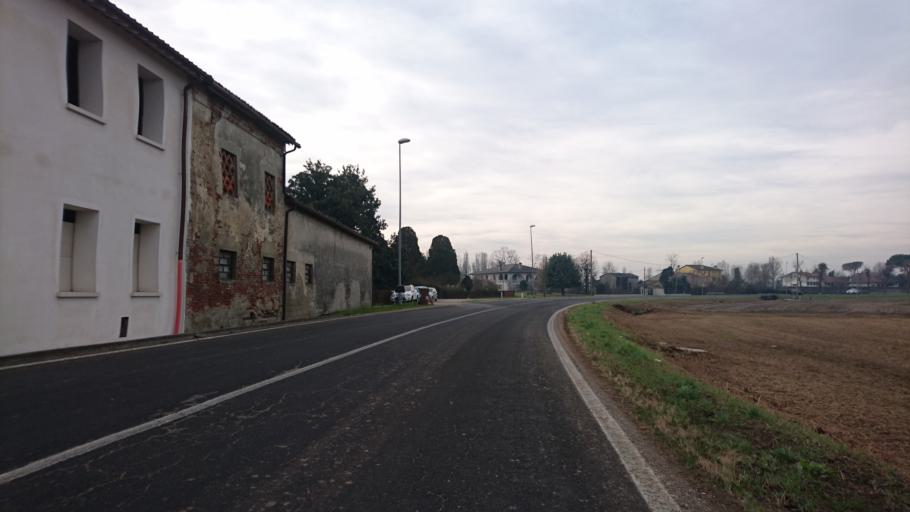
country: IT
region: Veneto
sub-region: Provincia di Padova
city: Campodoro
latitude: 45.4878
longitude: 11.7421
